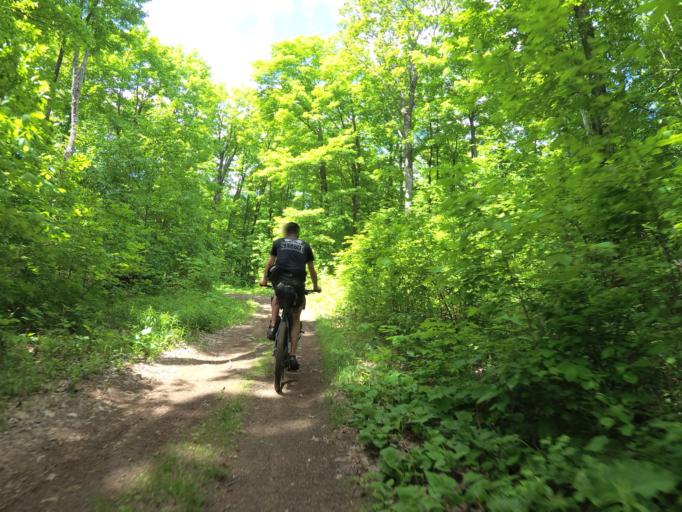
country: CA
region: Ontario
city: Renfrew
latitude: 45.0694
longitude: -76.7984
